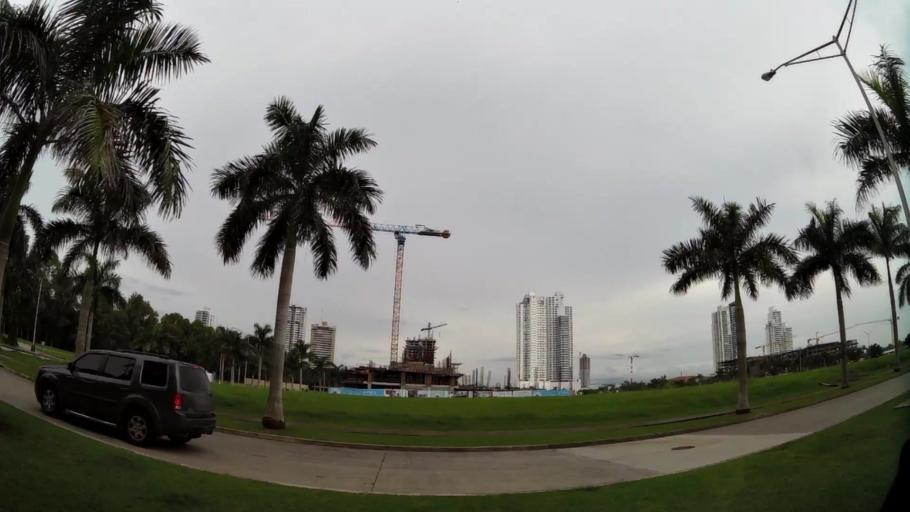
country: PA
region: Panama
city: San Miguelito
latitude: 9.0111
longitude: -79.4682
